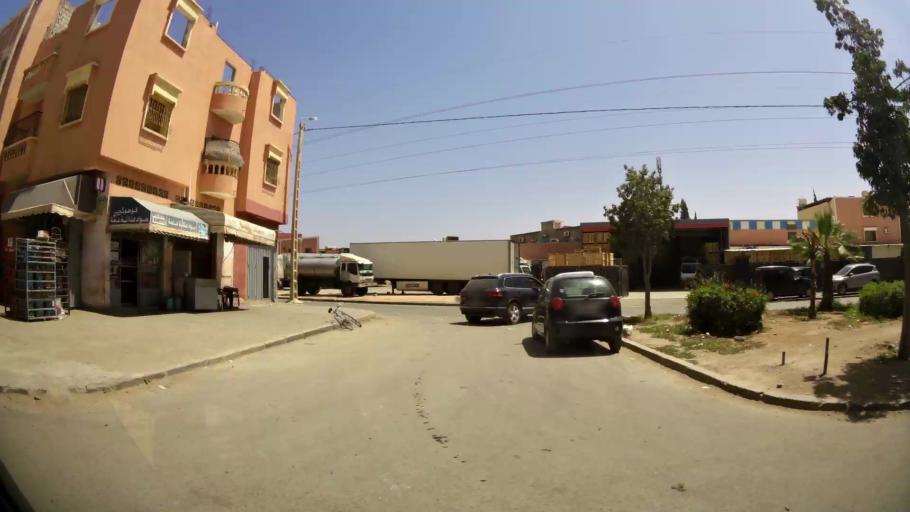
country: MA
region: Souss-Massa-Draa
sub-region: Inezgane-Ait Mellou
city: Inezgane
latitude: 30.3296
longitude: -9.4973
